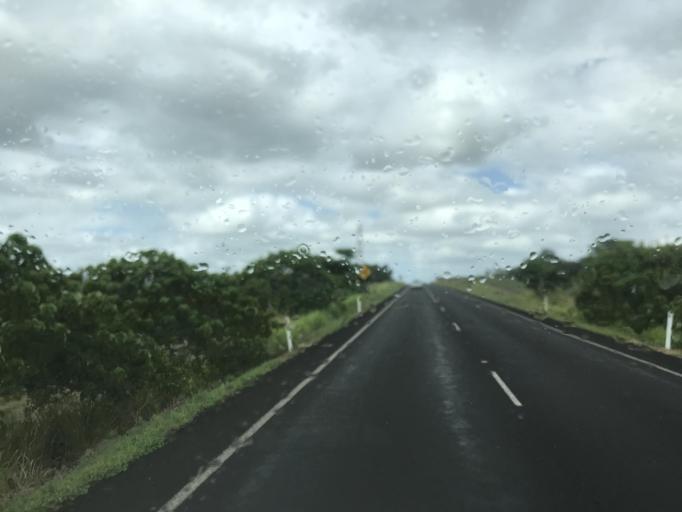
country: AU
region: Queensland
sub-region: Cassowary Coast
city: Innisfail
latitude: -17.5794
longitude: 145.9894
